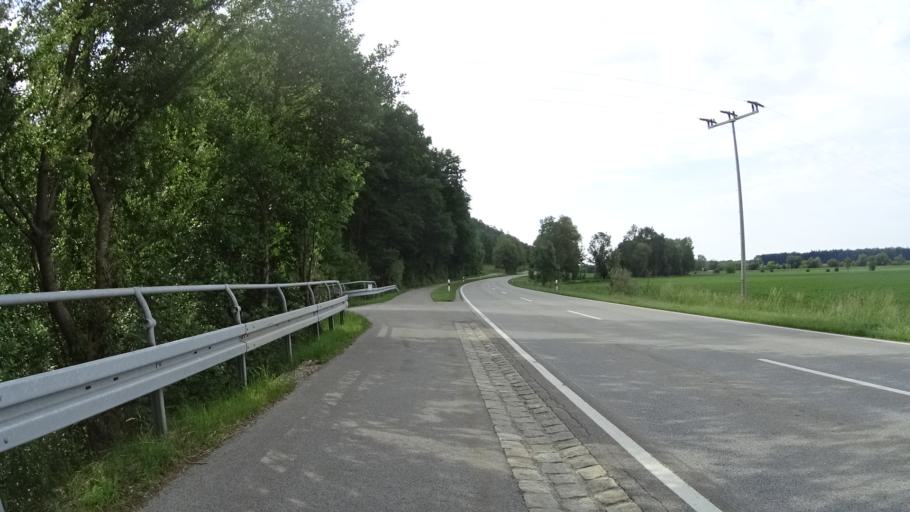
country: DE
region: Bavaria
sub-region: Lower Bavaria
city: Bogen
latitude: 48.8911
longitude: 12.7324
